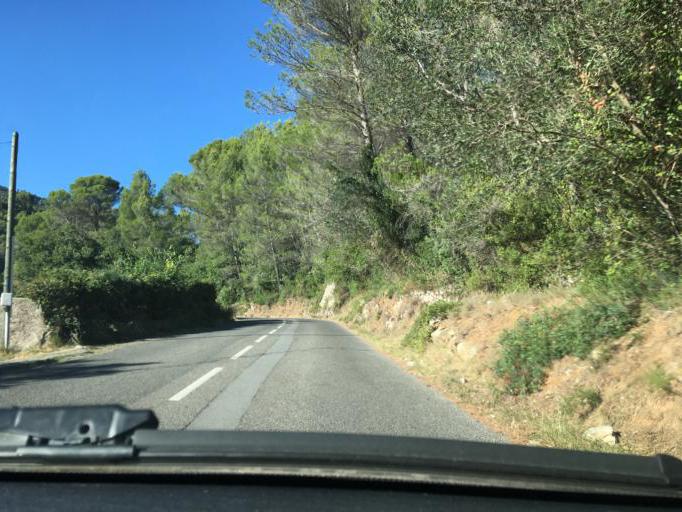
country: FR
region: Provence-Alpes-Cote d'Azur
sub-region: Departement du Var
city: Flayosc
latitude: 43.5685
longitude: 6.4230
